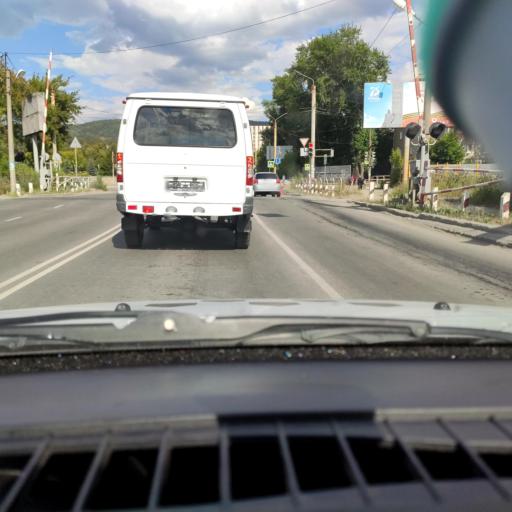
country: RU
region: Chelyabinsk
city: Miass
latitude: 55.0646
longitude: 60.1030
